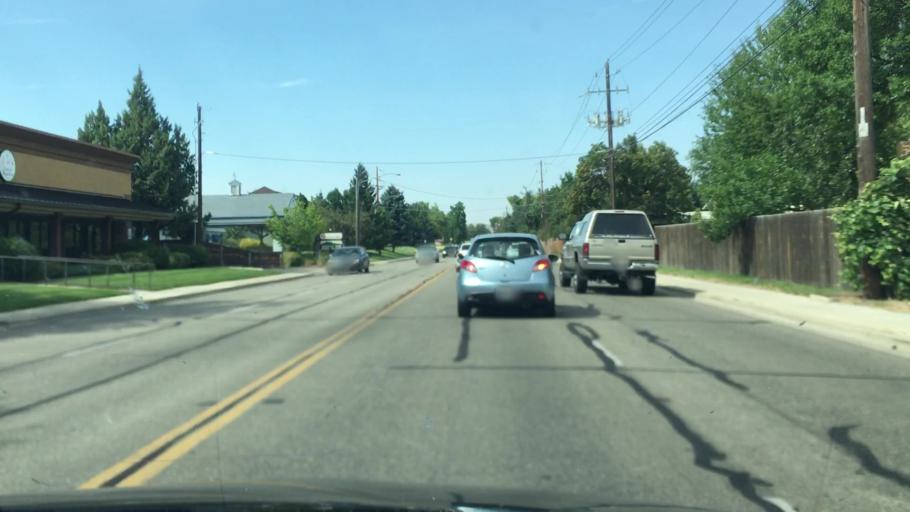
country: US
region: Idaho
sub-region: Ada County
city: Garden City
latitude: 43.6357
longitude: -116.2743
